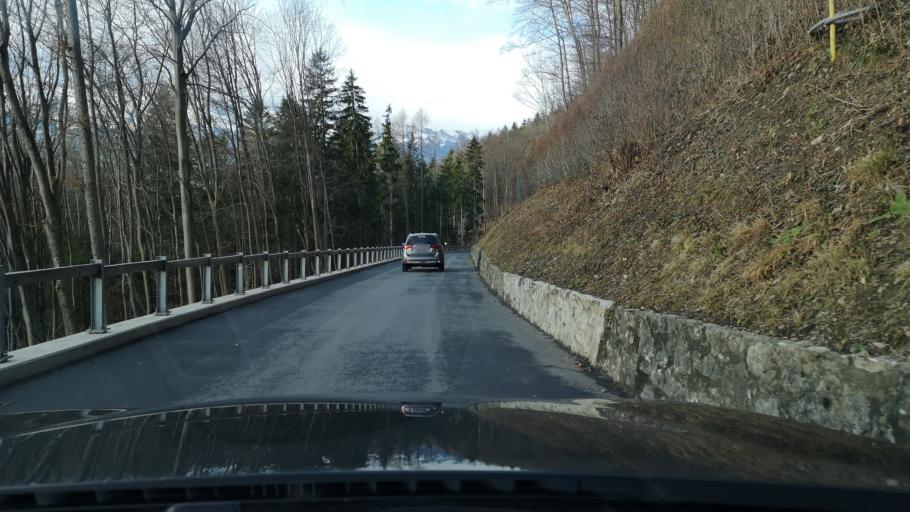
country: LI
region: Vaduz
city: Vaduz
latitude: 47.1322
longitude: 9.5297
